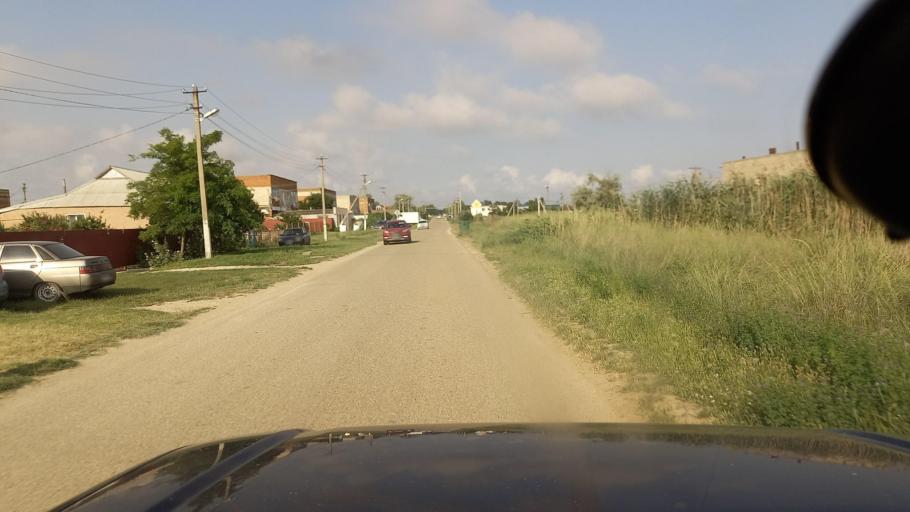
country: RU
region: Krasnodarskiy
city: Vyshestebliyevskaya
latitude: 45.1262
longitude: 36.8980
